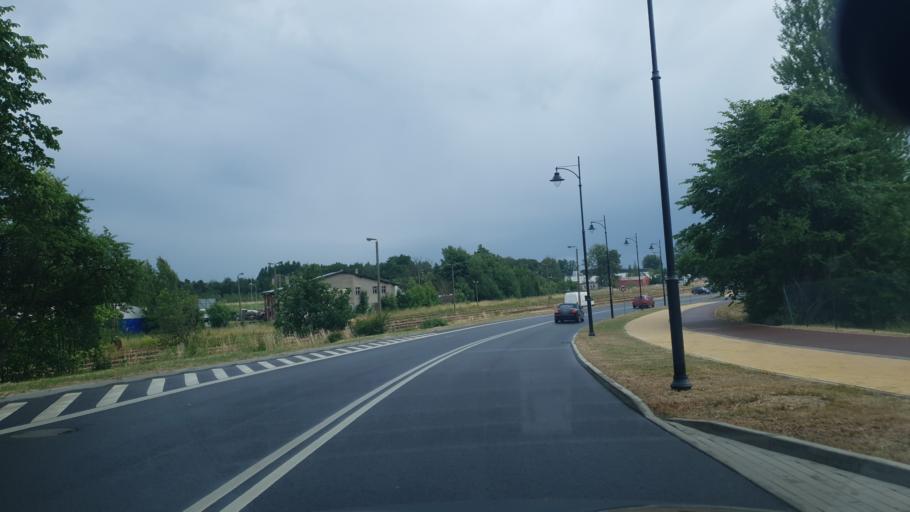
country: PL
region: Pomeranian Voivodeship
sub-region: Powiat kartuski
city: Kartuzy
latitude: 54.3379
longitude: 18.2073
